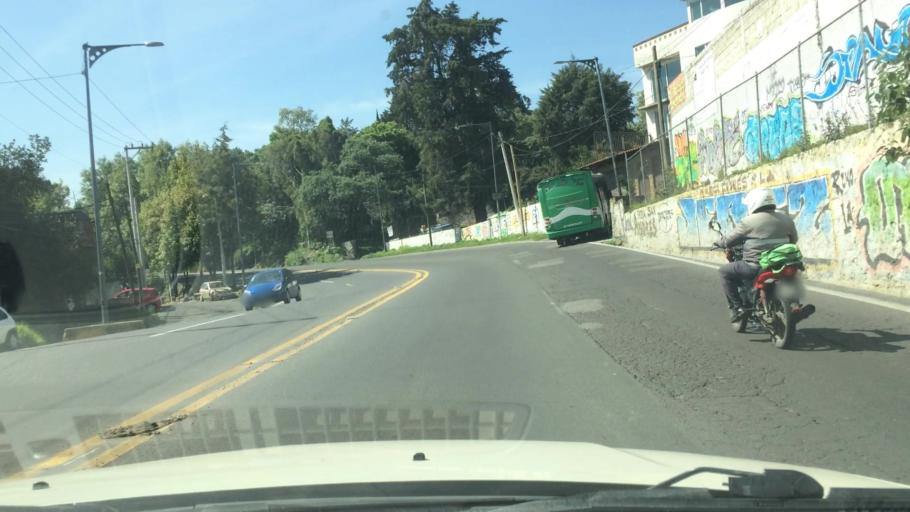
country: MX
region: Mexico City
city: Tlalpan
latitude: 19.2484
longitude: -99.1724
